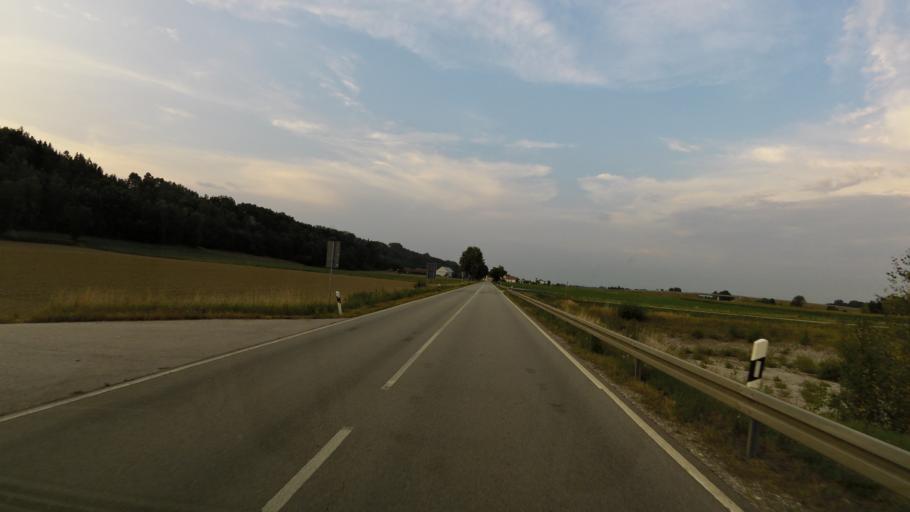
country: DE
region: Bavaria
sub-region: Lower Bavaria
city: Rotthalmunster
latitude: 48.3298
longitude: 13.2223
